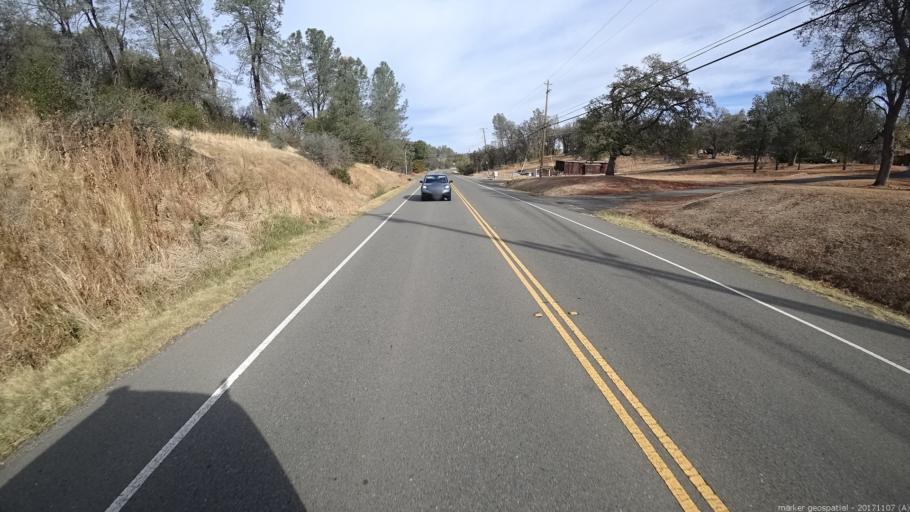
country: US
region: California
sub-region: Shasta County
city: Shasta
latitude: 40.5303
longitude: -122.4754
